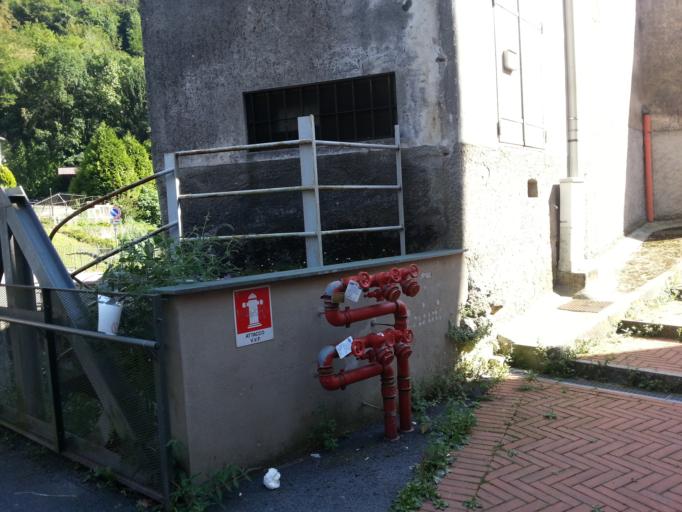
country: IT
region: Lombardy
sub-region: Provincia di Lecco
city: Lecco
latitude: 45.8752
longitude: 9.4048
